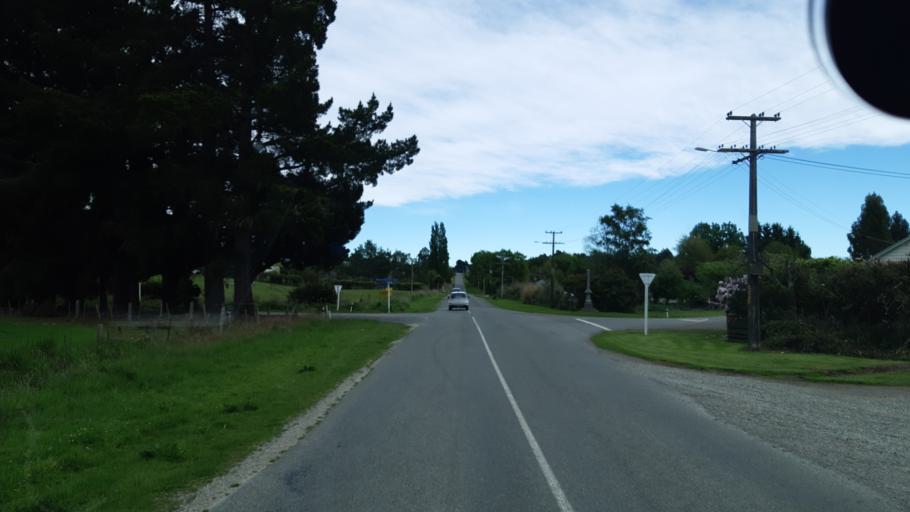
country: NZ
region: Canterbury
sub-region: Timaru District
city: Timaru
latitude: -44.4398
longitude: 171.1636
